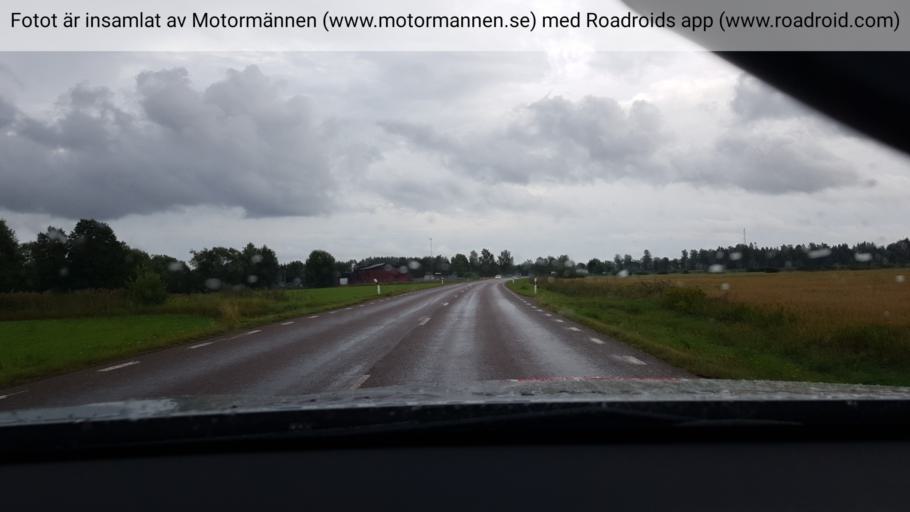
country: SE
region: Uppsala
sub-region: Tierps Kommun
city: Karlholmsbruk
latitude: 60.4820
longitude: 17.7477
